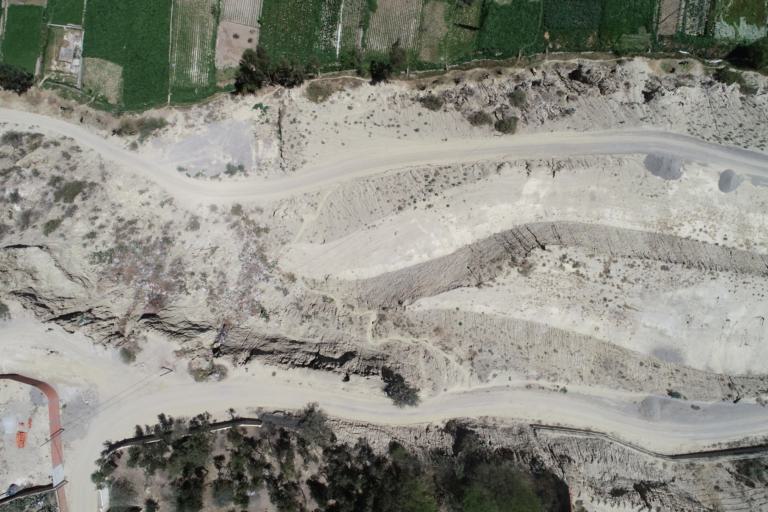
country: BO
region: La Paz
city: La Paz
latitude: -16.6458
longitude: -68.0461
